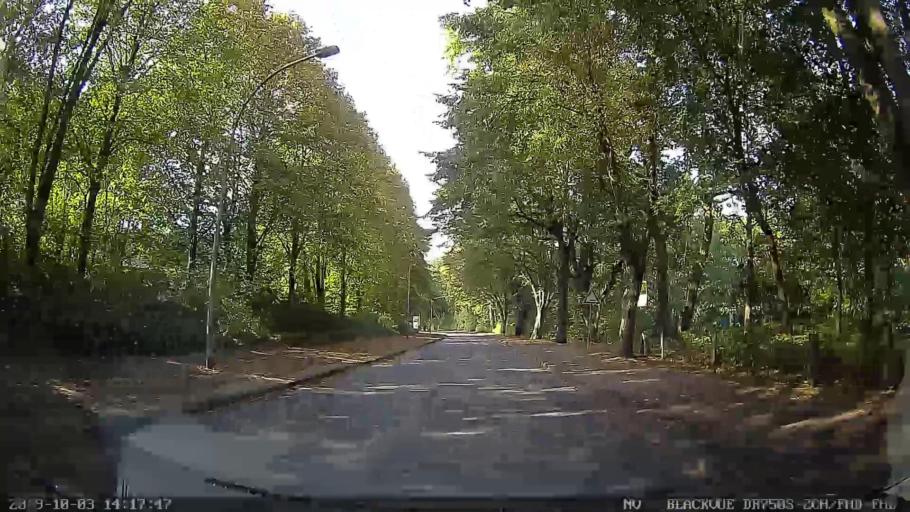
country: DE
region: Schleswig-Holstein
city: Pinneberg
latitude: 53.6631
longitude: 9.8041
